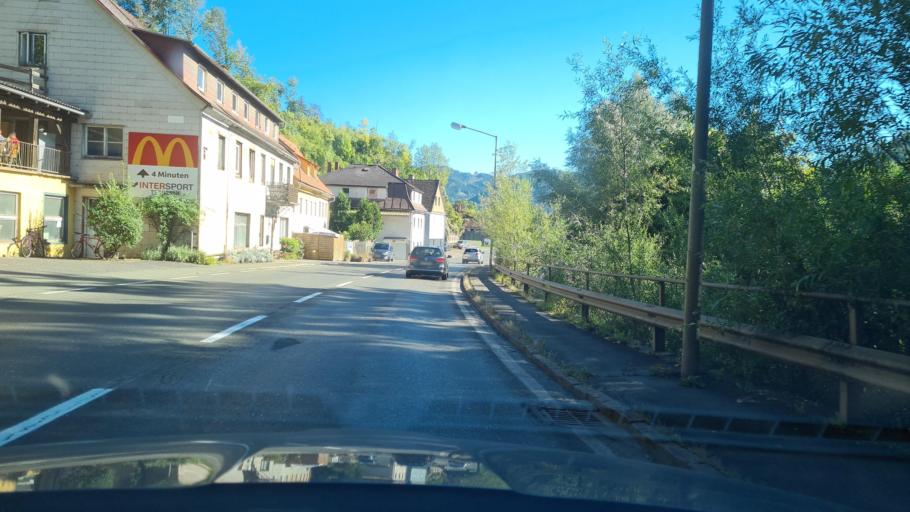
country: AT
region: Styria
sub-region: Politischer Bezirk Leoben
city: Leoben
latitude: 47.3785
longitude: 15.0792
